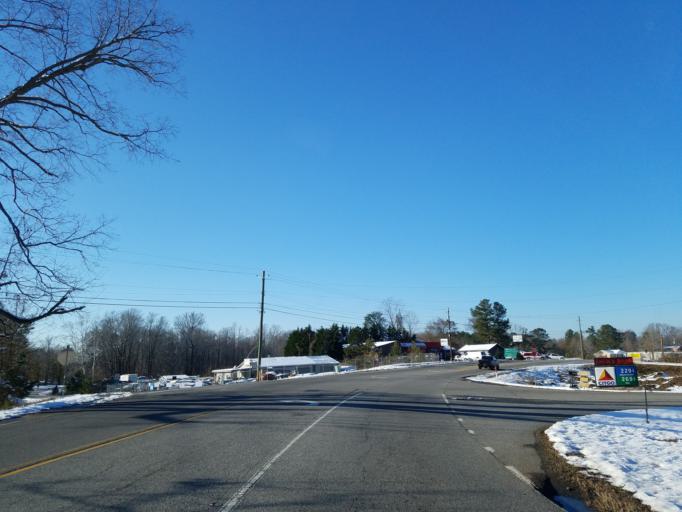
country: US
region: Georgia
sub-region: Dawson County
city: Dawsonville
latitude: 34.3351
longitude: -84.1180
